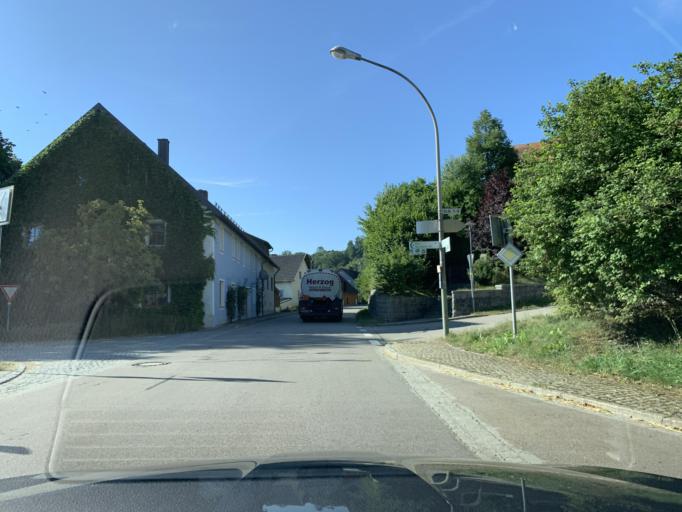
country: DE
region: Bavaria
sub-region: Upper Palatinate
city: Pettendorf
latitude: 49.3523
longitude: 12.3626
